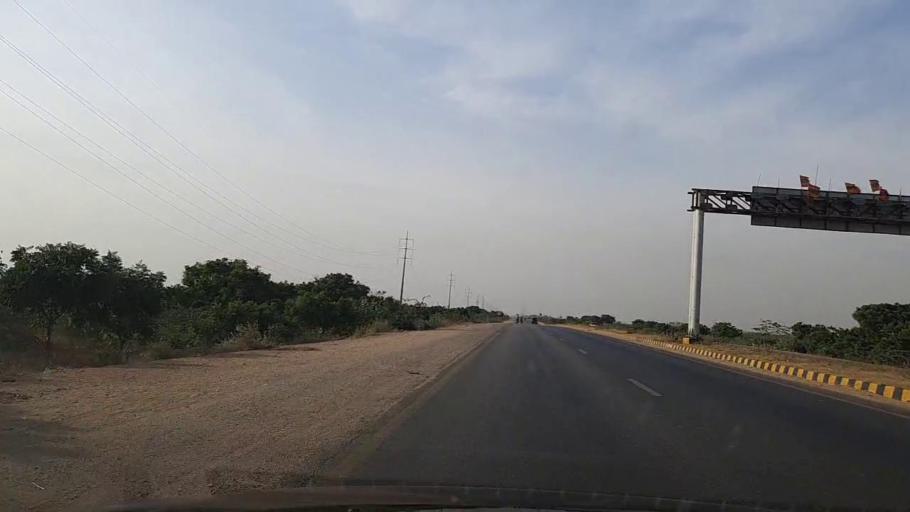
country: PK
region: Sindh
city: Gharo
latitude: 24.7710
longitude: 67.5468
